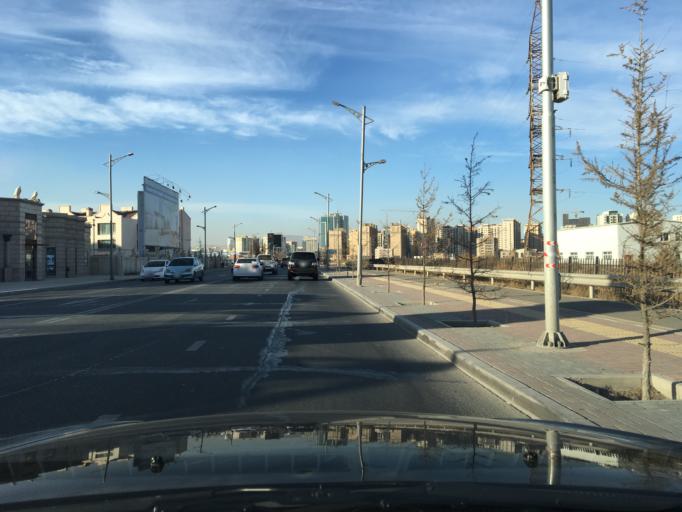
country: MN
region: Ulaanbaatar
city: Ulaanbaatar
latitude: 47.8945
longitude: 106.9354
